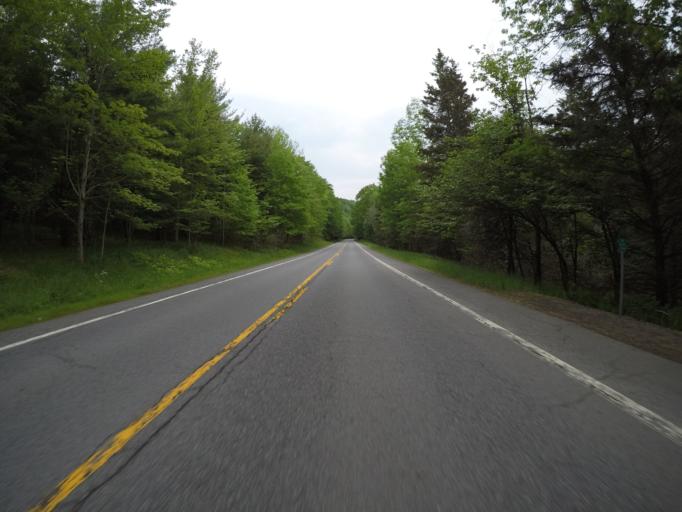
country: US
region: New York
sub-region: Sullivan County
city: Livingston Manor
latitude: 42.0758
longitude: -74.8743
